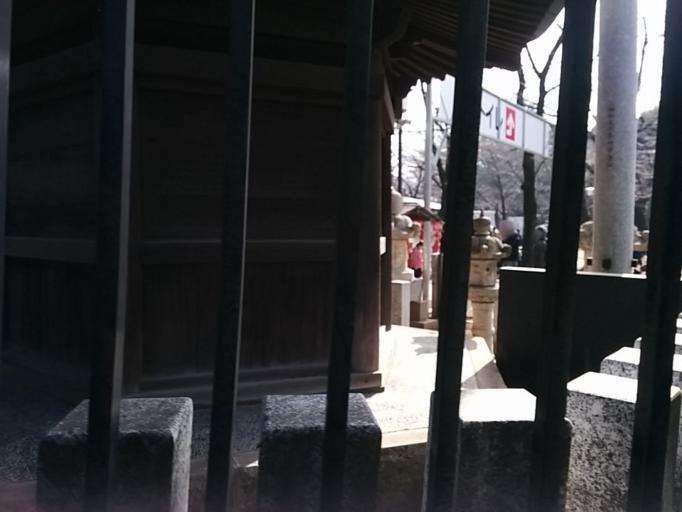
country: JP
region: Saitama
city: Kawagoe
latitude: 35.9180
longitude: 139.4898
